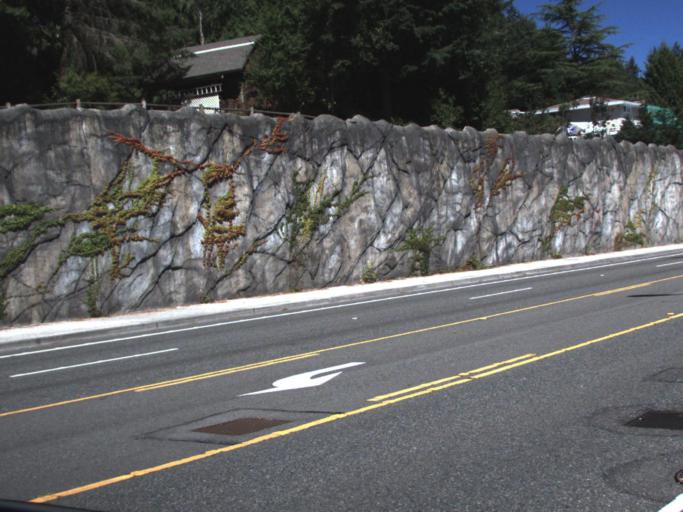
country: US
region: Washington
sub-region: King County
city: Issaquah
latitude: 47.5332
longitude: -122.0622
